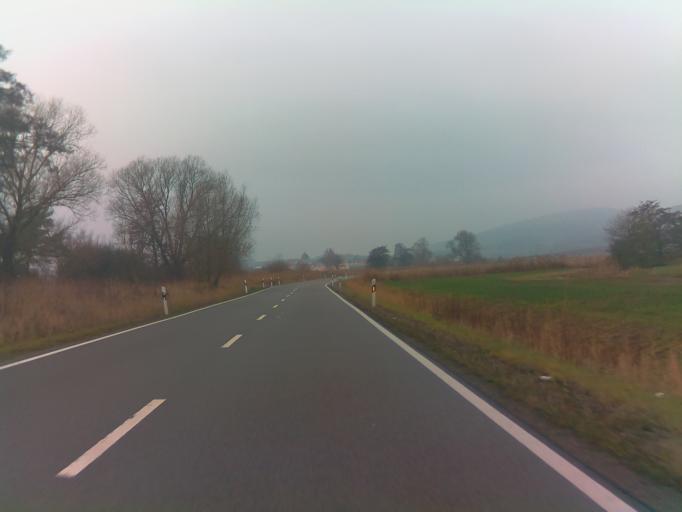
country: DE
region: Thuringia
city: Romhild
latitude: 50.4237
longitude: 10.5176
